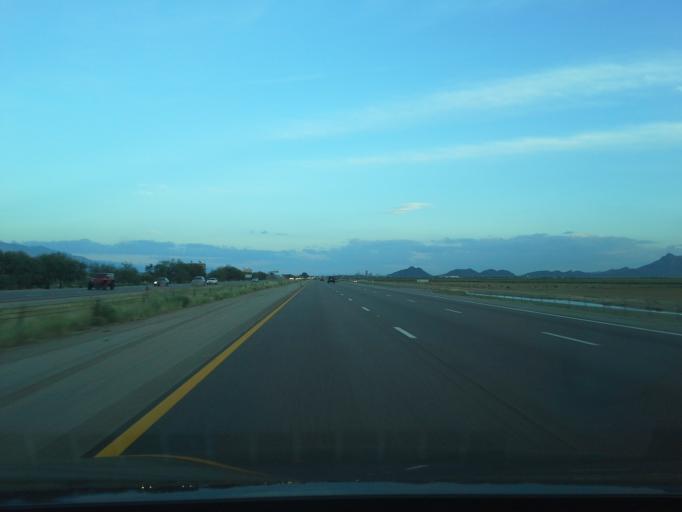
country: US
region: Arizona
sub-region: Pima County
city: Marana
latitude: 32.4504
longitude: -111.2000
